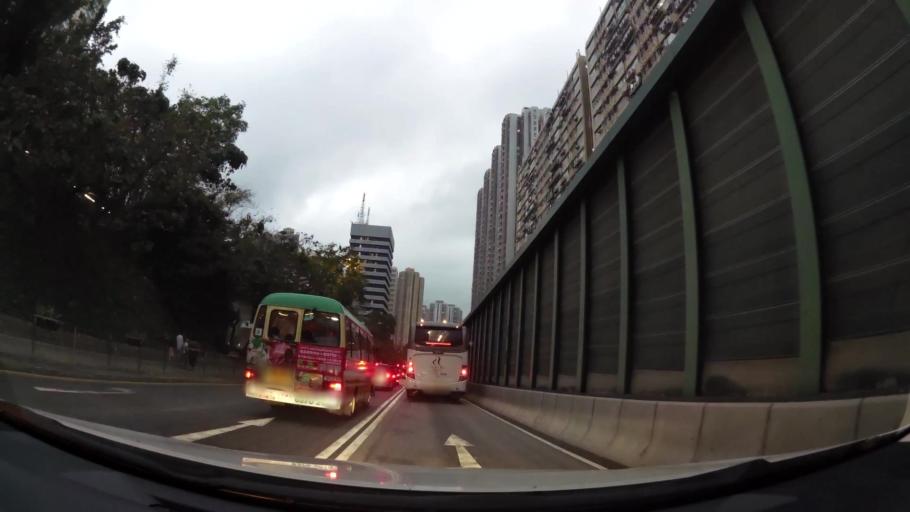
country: HK
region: Tsuen Wan
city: Tsuen Wan
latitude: 22.3500
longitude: 114.1091
